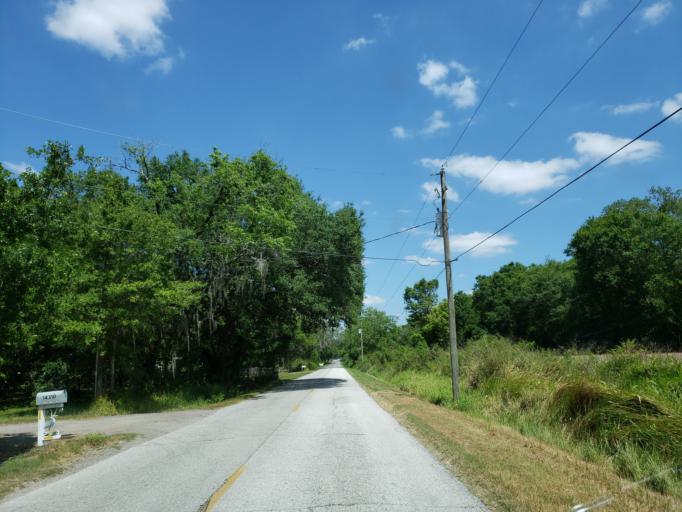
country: US
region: Florida
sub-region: Hillsborough County
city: Valrico
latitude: 27.9587
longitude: -82.2173
